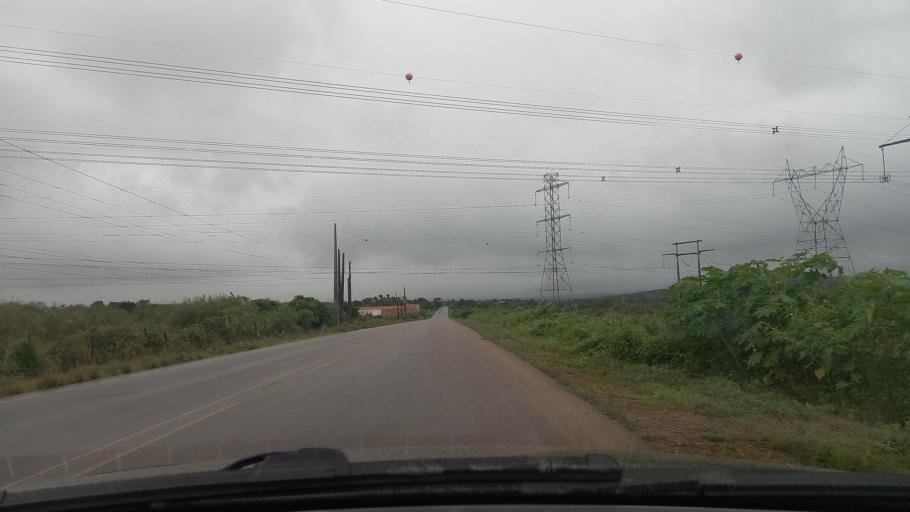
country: BR
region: Alagoas
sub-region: Delmiro Gouveia
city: Delmiro Gouveia
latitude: -9.3280
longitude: -37.9830
